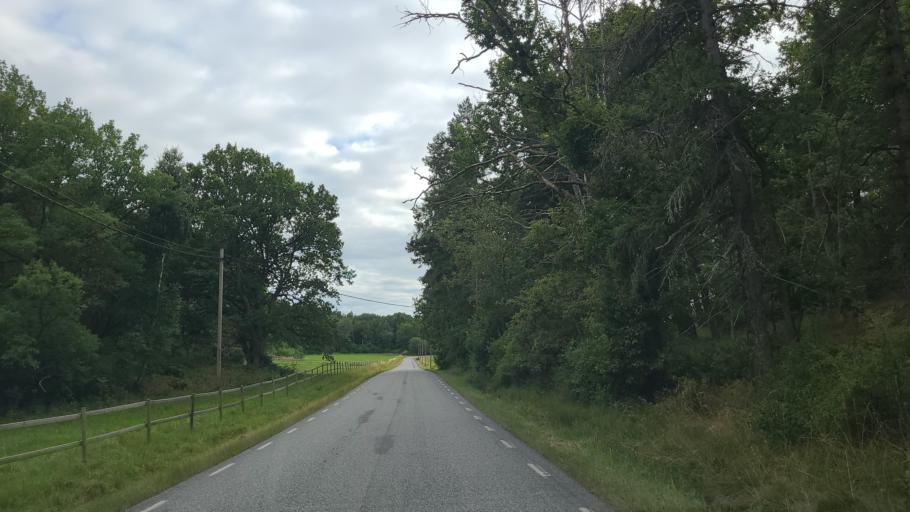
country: SE
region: Stockholm
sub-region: Upplands-Bro Kommun
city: Bro
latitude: 59.4752
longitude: 17.5962
